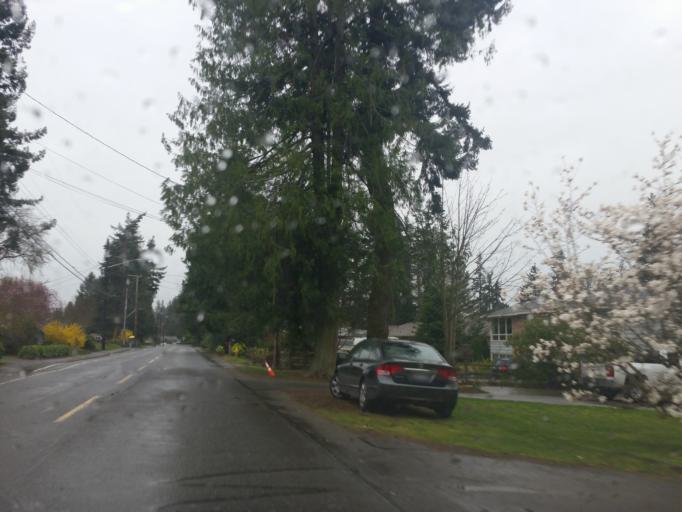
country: US
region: Washington
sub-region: Snohomish County
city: Lynnwood
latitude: 47.8238
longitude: -122.3468
